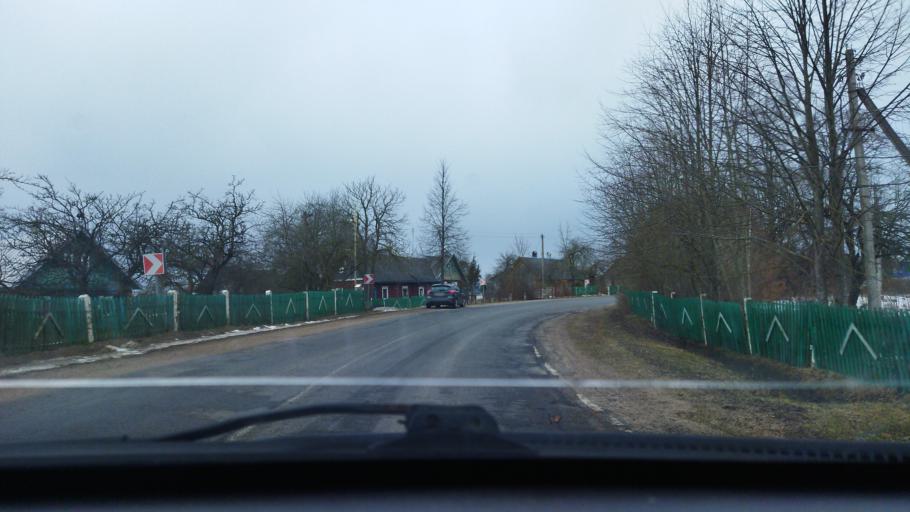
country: BY
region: Minsk
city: Svir
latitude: 54.8757
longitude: 26.3930
